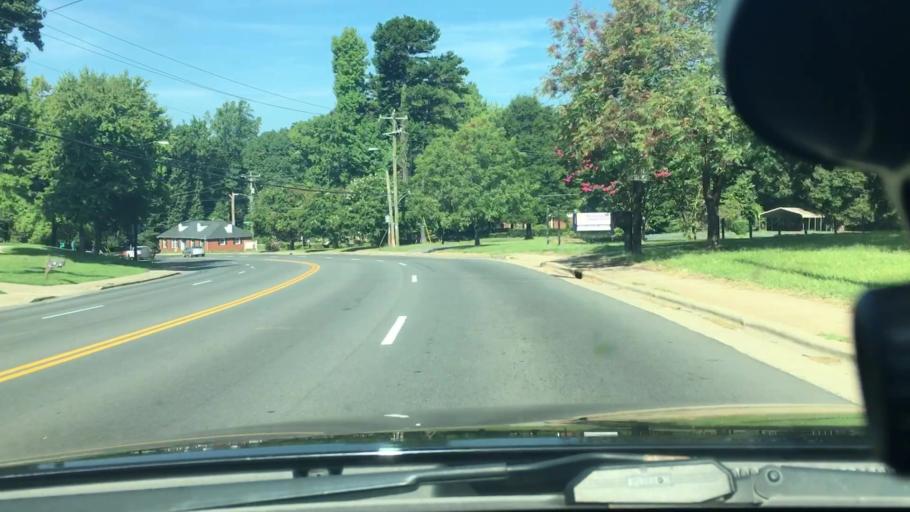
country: US
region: North Carolina
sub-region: Mecklenburg County
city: Matthews
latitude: 35.1874
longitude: -80.7344
